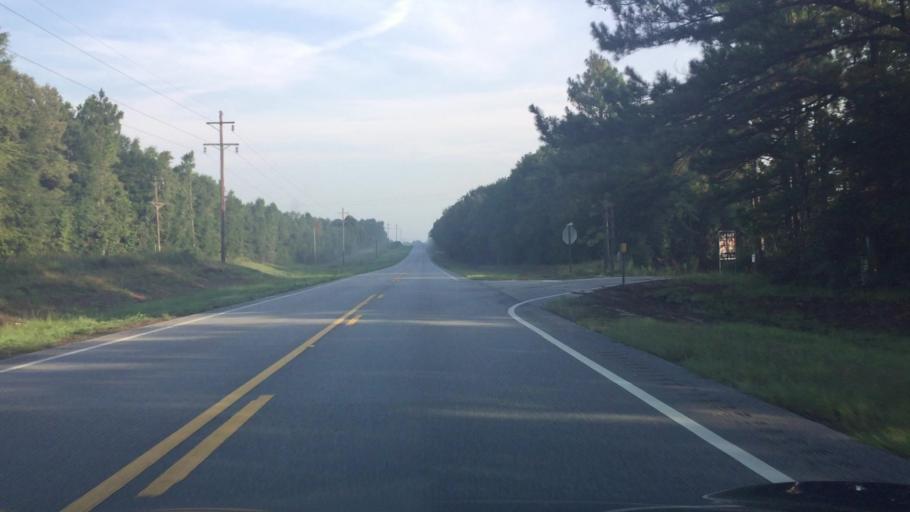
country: US
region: Alabama
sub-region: Covington County
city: Florala
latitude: 31.0642
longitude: -86.3979
